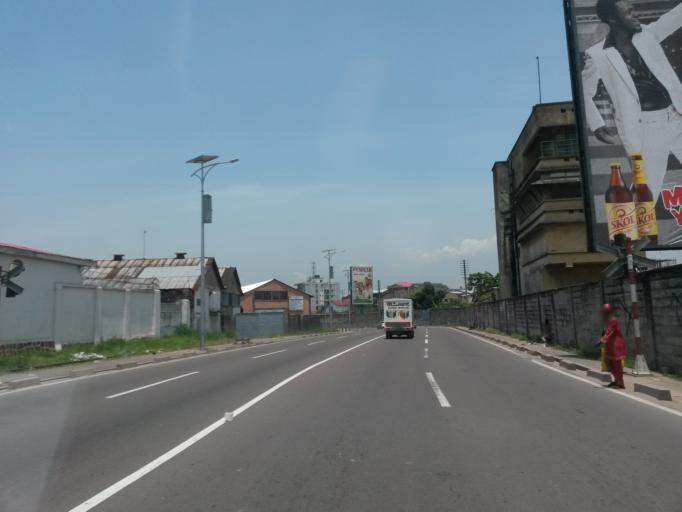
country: CD
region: Kinshasa
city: Kinshasa
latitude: -4.3024
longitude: 15.3216
